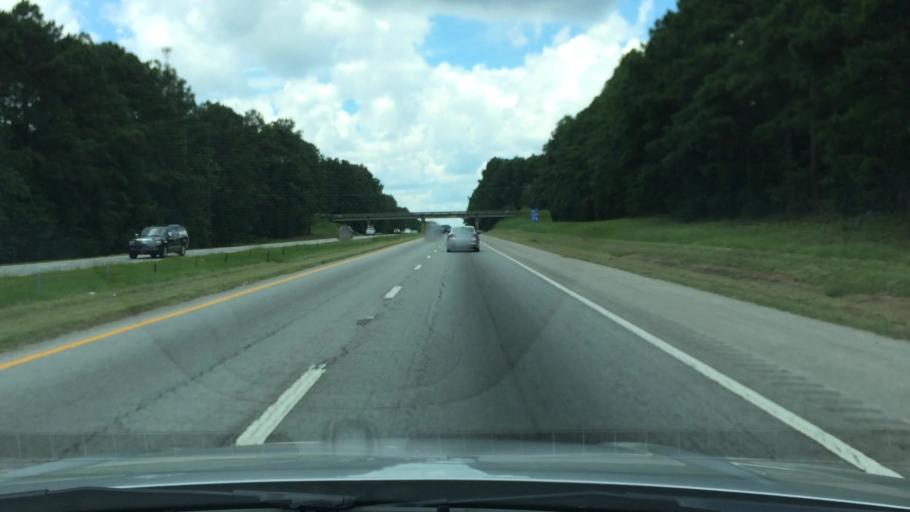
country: US
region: South Carolina
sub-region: Newberry County
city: Newberry
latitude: 34.3152
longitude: -81.5813
